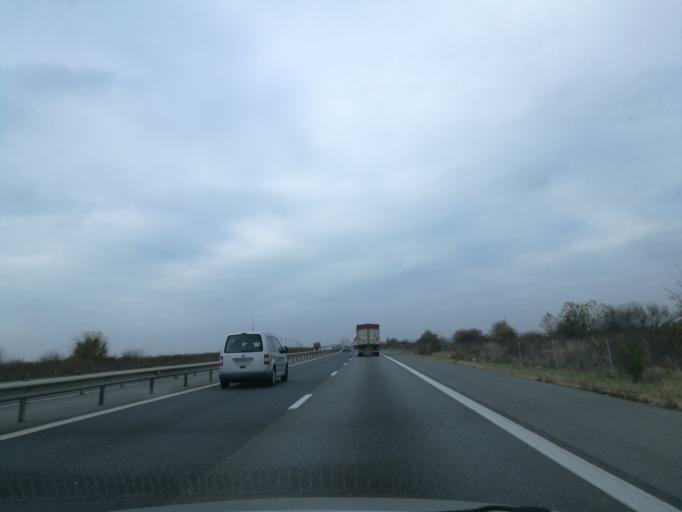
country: RO
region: Giurgiu
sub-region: Comuna Joita
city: Joita
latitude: 44.4665
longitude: 25.8594
